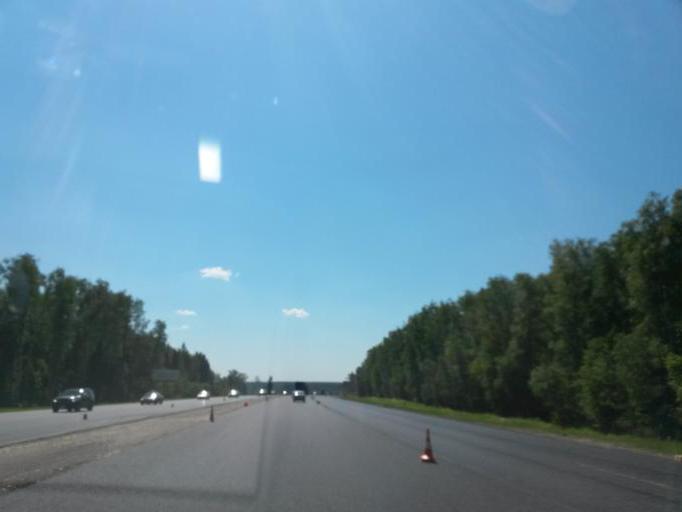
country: RU
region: Moskovskaya
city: Novyy Byt
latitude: 55.0954
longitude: 37.5852
